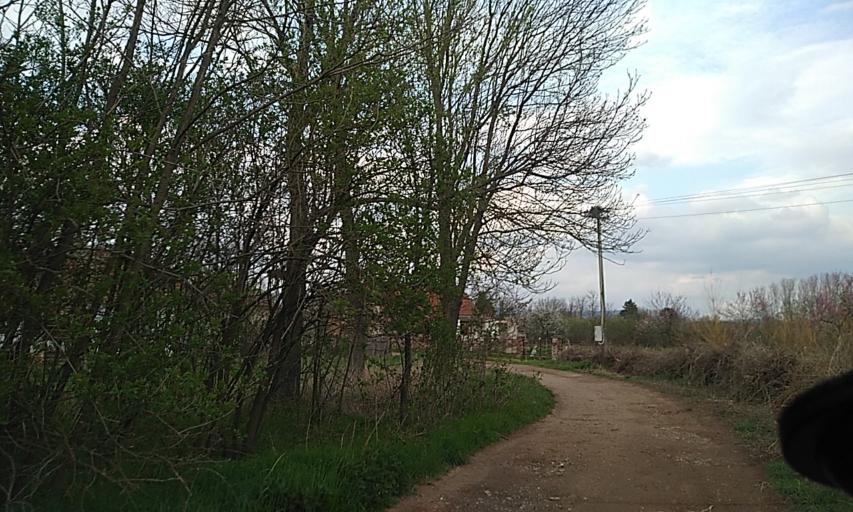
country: RS
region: Central Serbia
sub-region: Nisavski Okrug
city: Razanj
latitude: 43.5941
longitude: 21.6076
